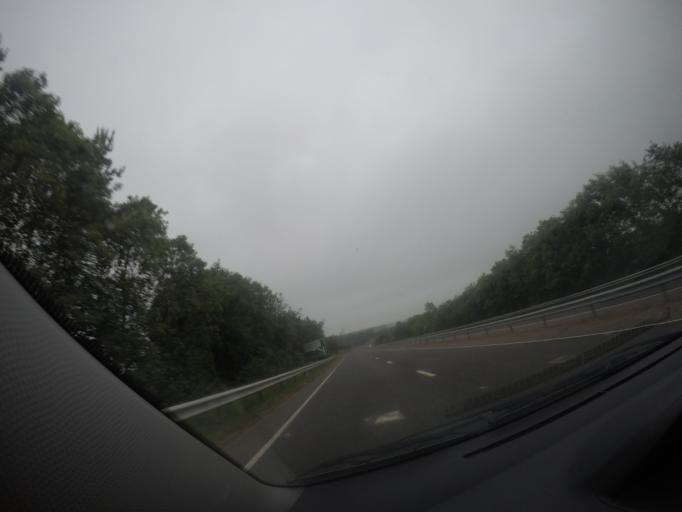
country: GB
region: Scotland
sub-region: Angus
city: Forfar
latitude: 56.5901
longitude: -2.9126
